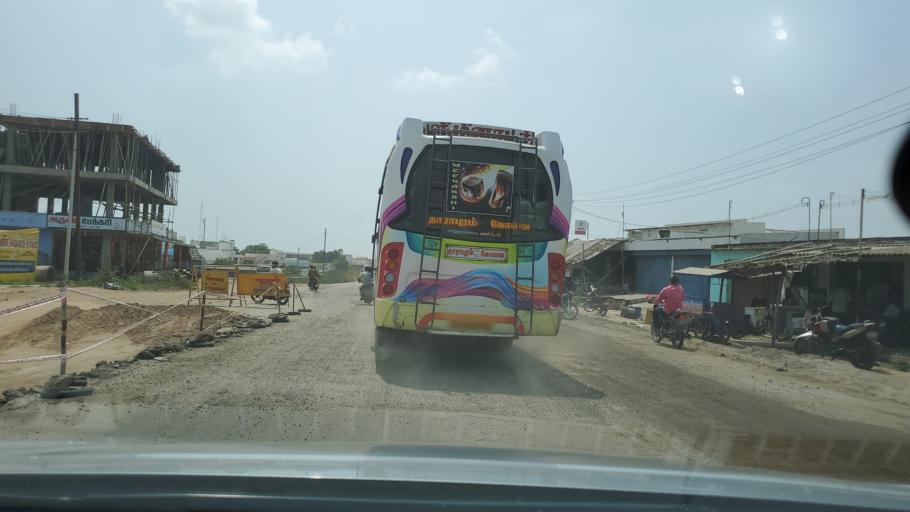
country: IN
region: Tamil Nadu
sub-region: Tiruppur
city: Dharapuram
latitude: 10.7392
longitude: 77.5178
